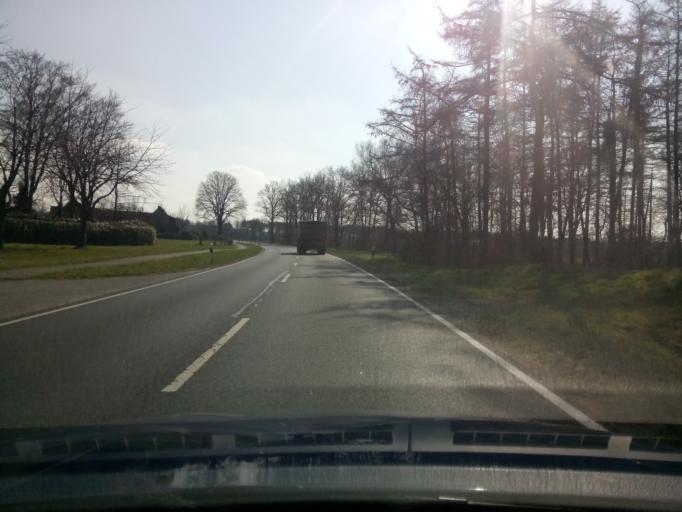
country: DE
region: Lower Saxony
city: Isterberg
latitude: 52.3466
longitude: 7.0742
